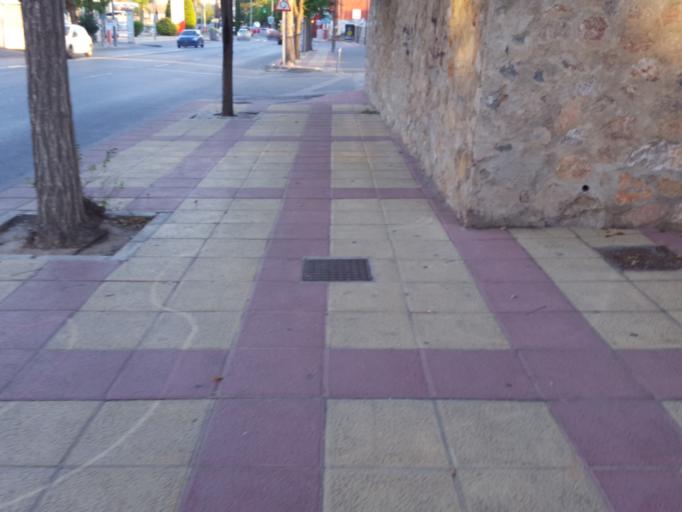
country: ES
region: Murcia
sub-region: Murcia
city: Murcia
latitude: 38.0045
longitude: -1.1480
